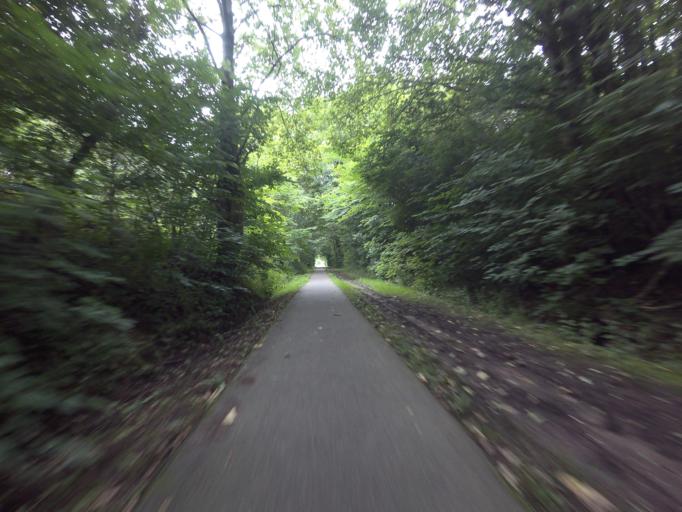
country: DK
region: Central Jutland
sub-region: Horsens Kommune
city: Braedstrup
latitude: 55.9777
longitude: 9.5982
